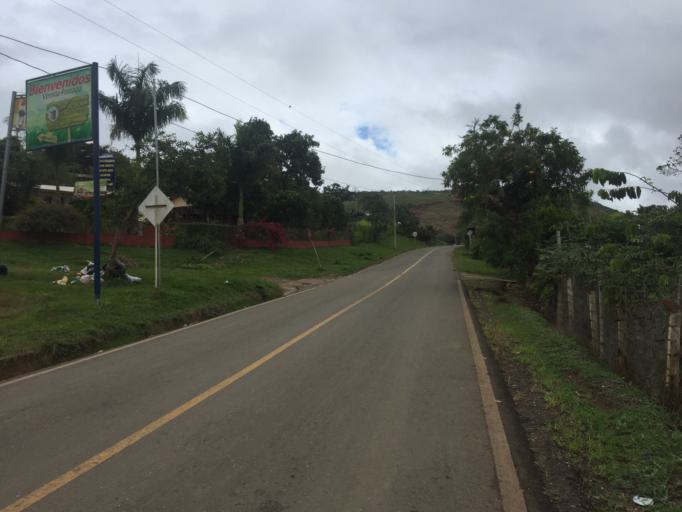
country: CO
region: Valle del Cauca
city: Dagua
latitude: 3.6863
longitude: -76.5926
